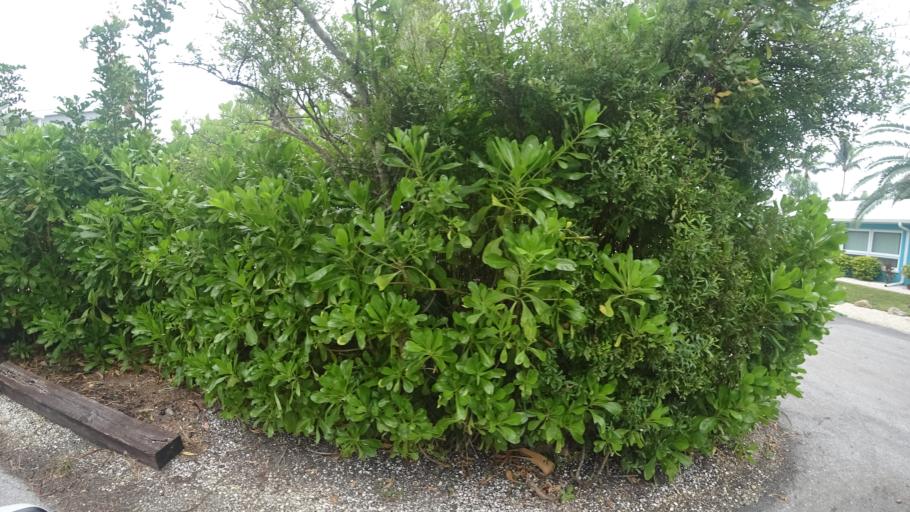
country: US
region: Florida
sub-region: Manatee County
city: Bradenton Beach
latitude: 27.4723
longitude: -82.6996
